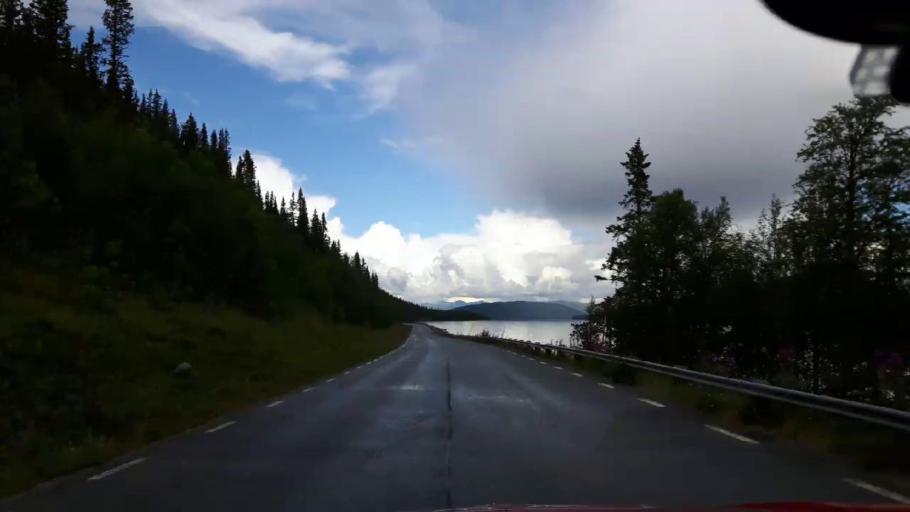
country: SE
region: Vaesterbotten
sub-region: Vilhelmina Kommun
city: Sjoberg
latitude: 64.9784
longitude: 15.3154
